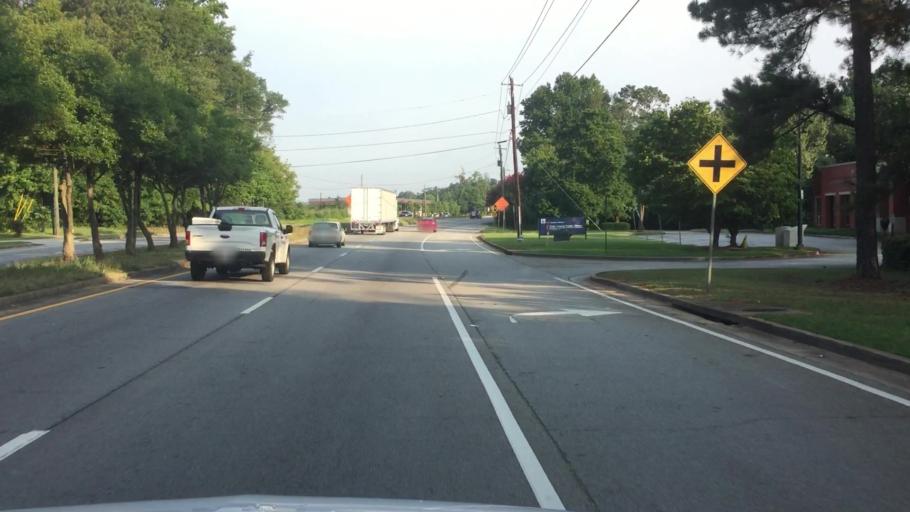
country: US
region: Georgia
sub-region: DeKalb County
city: Panthersville
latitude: 33.6908
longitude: -84.2581
